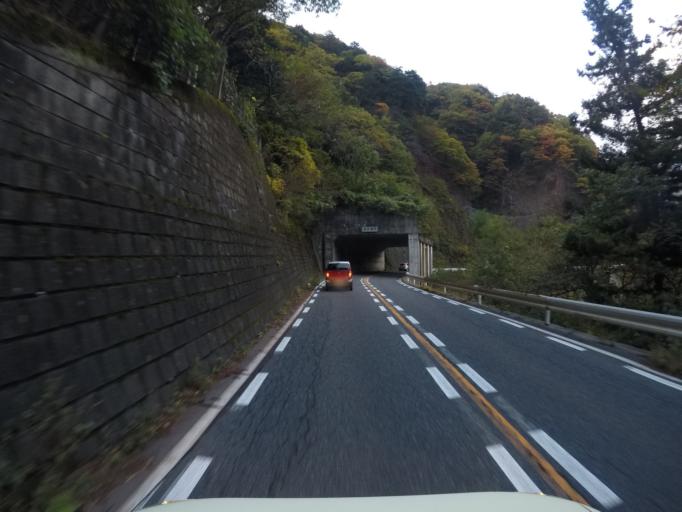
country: JP
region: Nagano
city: Toyoshina
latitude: 36.1727
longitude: 137.7789
